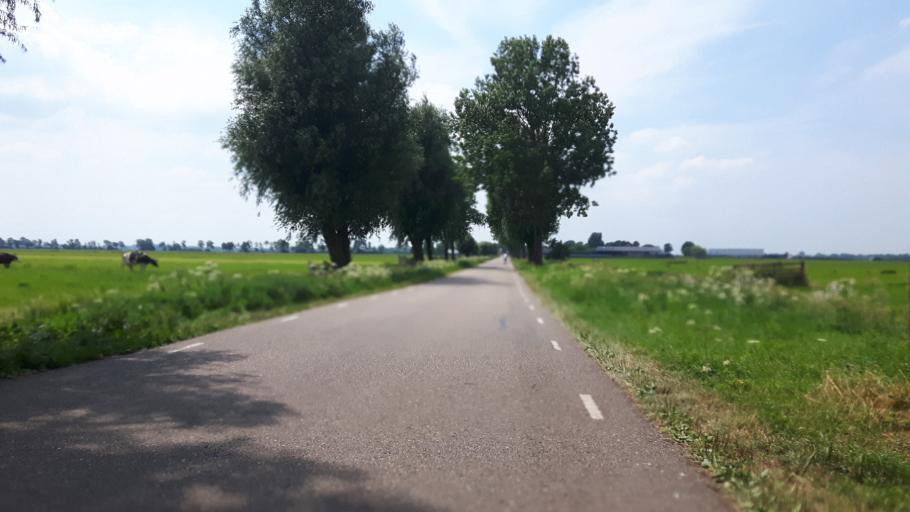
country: NL
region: Utrecht
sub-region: Gemeente Lopik
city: Lopik
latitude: 51.9163
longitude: 4.9298
